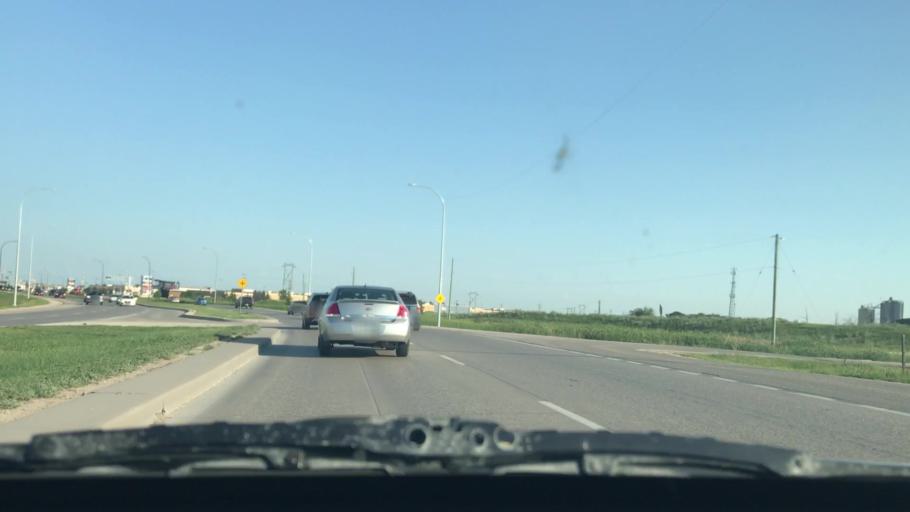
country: CA
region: Manitoba
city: Winnipeg
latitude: 49.8296
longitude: -97.2094
